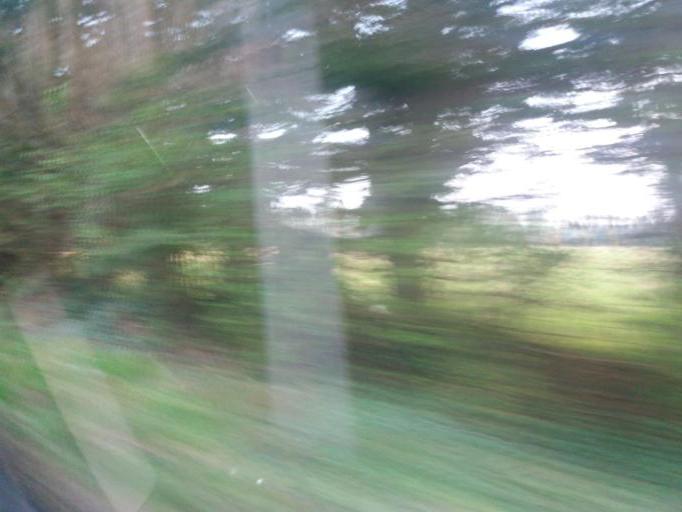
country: IE
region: Leinster
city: Hartstown
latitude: 53.3871
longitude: -6.4291
